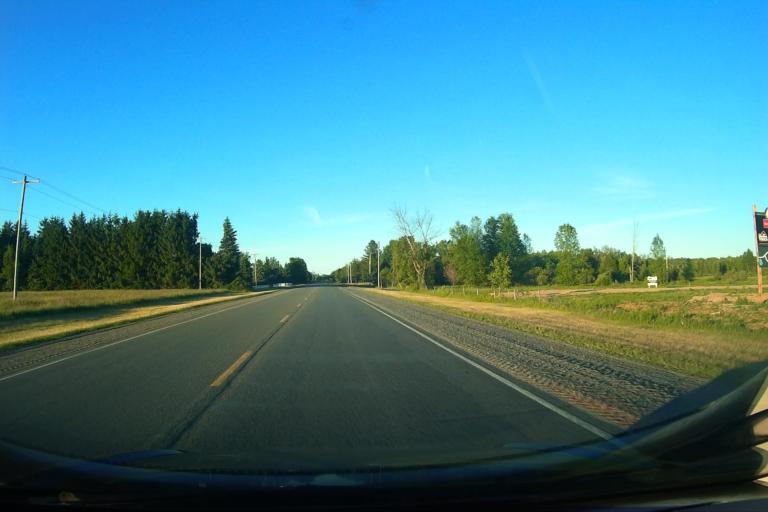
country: CA
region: Ontario
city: Prescott
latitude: 45.0426
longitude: -75.5846
